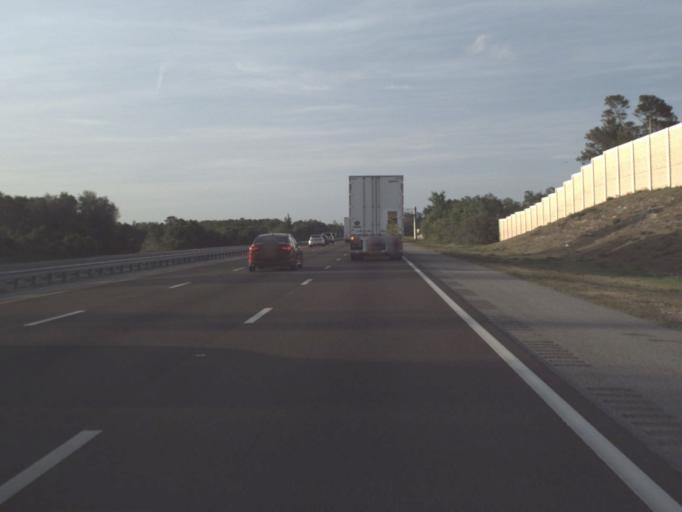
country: US
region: Florida
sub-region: Brevard County
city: Titusville
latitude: 28.5939
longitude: -80.8512
